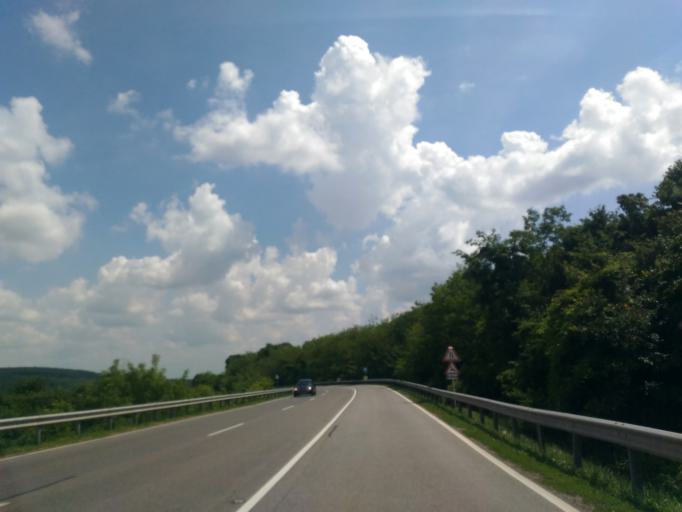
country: HU
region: Baranya
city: Pecs
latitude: 46.1285
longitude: 18.2541
